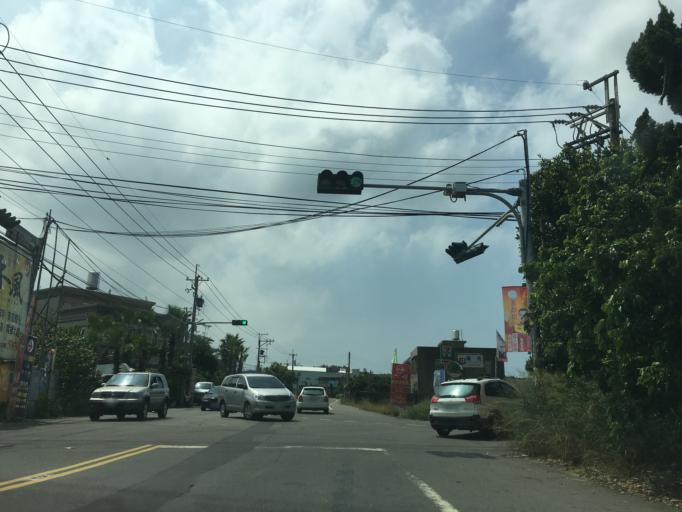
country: TW
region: Taiwan
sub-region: Hsinchu
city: Zhubei
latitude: 24.8935
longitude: 120.9767
